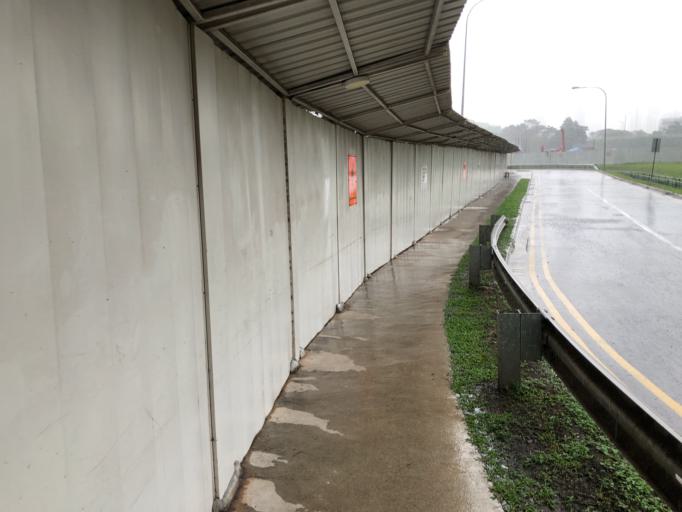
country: SG
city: Singapore
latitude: 1.2825
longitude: 103.8387
